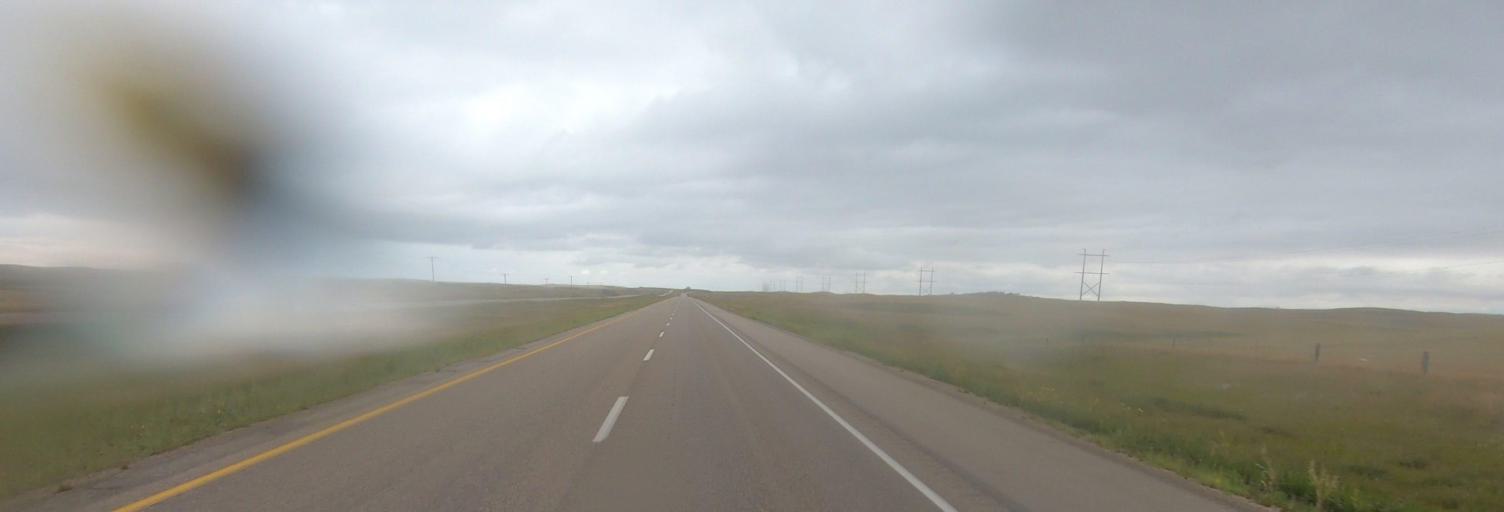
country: CA
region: Saskatchewan
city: Gravelbourg
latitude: 50.4631
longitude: -106.4067
